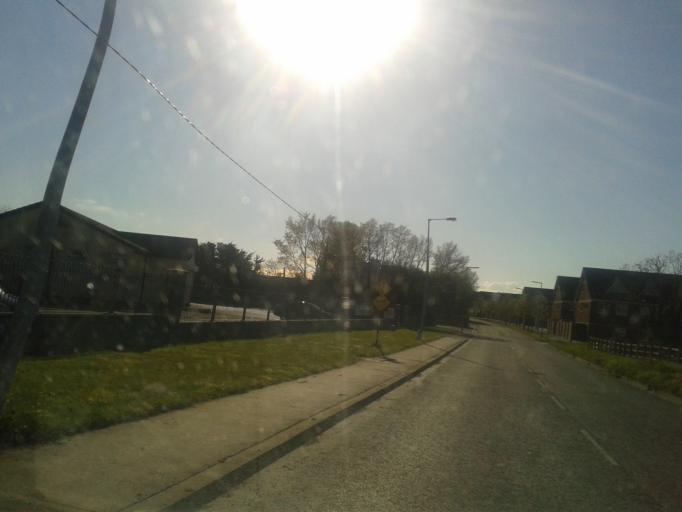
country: IE
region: Leinster
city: Kinsealy-Drinan
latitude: 53.4414
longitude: -6.1945
